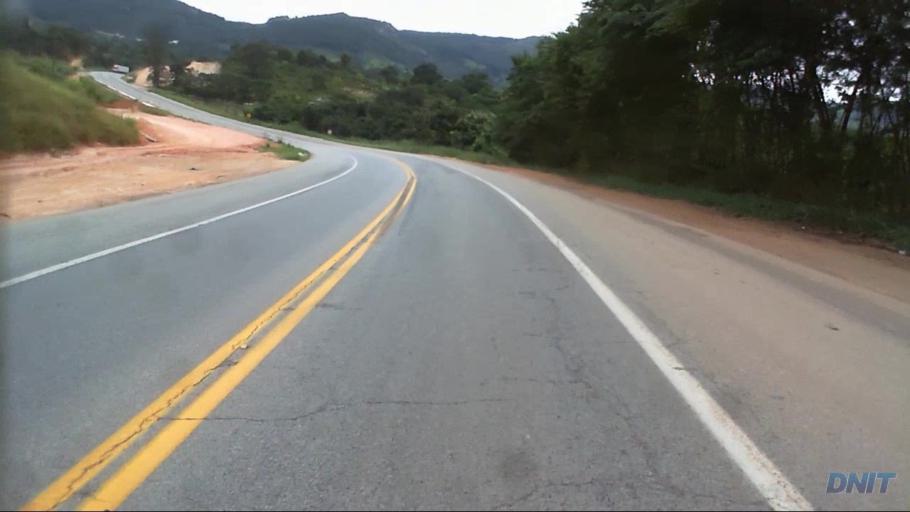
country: BR
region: Minas Gerais
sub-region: Barao De Cocais
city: Barao de Cocais
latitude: -19.7430
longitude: -43.4994
